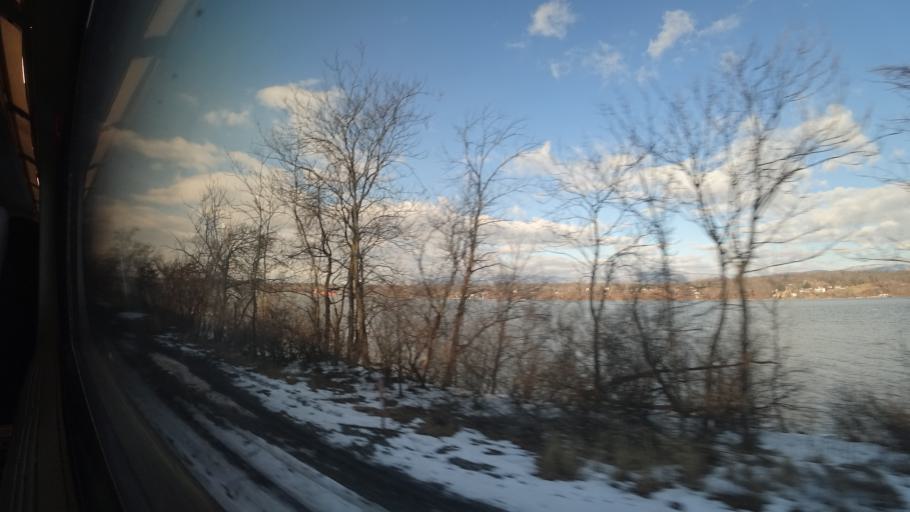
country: US
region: New York
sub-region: Ulster County
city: Saugerties
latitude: 42.1175
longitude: -73.9105
